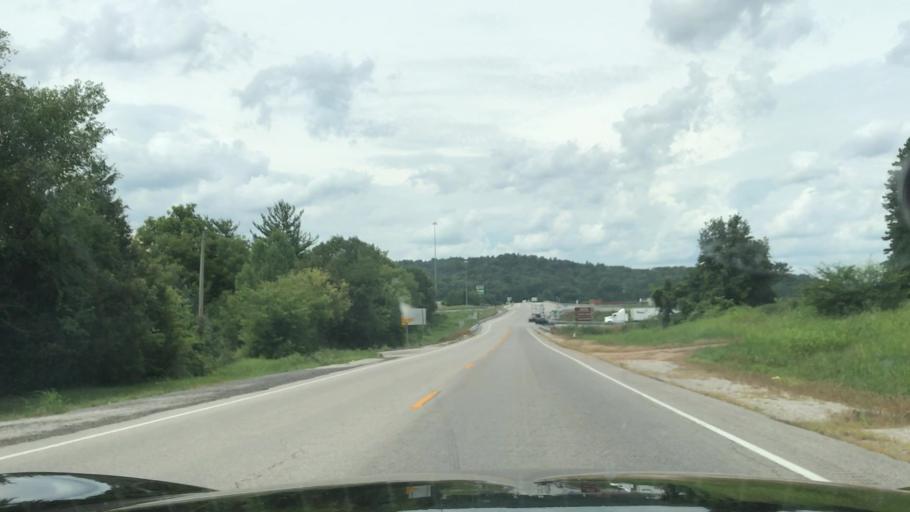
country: US
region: Kentucky
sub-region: Hart County
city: Horse Cave
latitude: 37.1988
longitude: -85.9331
